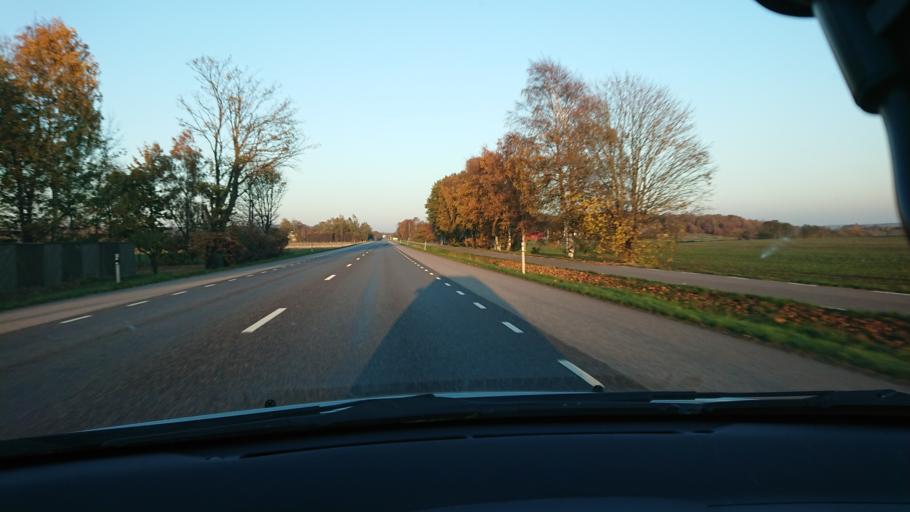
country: SE
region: Halland
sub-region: Halmstads Kommun
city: Fyllinge
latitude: 56.6885
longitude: 12.9584
